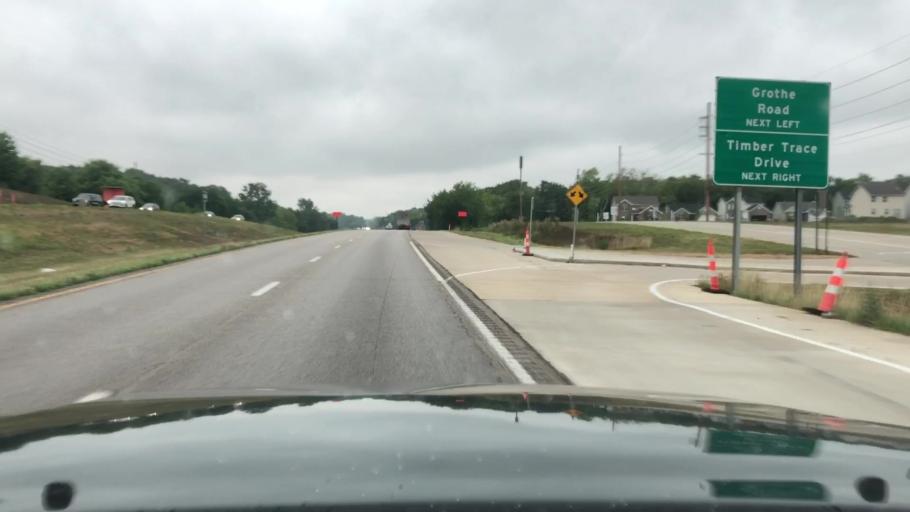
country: US
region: Missouri
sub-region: Saint Charles County
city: Wentzville
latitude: 38.8492
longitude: -90.8668
